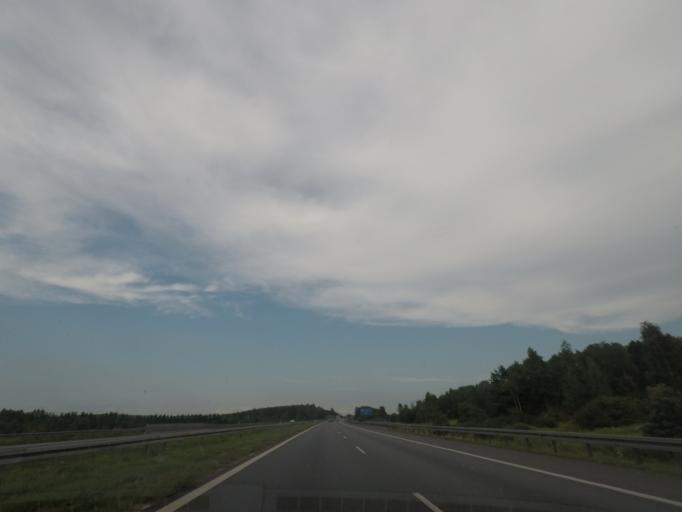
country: PL
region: Lesser Poland Voivodeship
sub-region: Powiat chrzanowski
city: Balin
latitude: 50.1530
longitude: 19.3592
